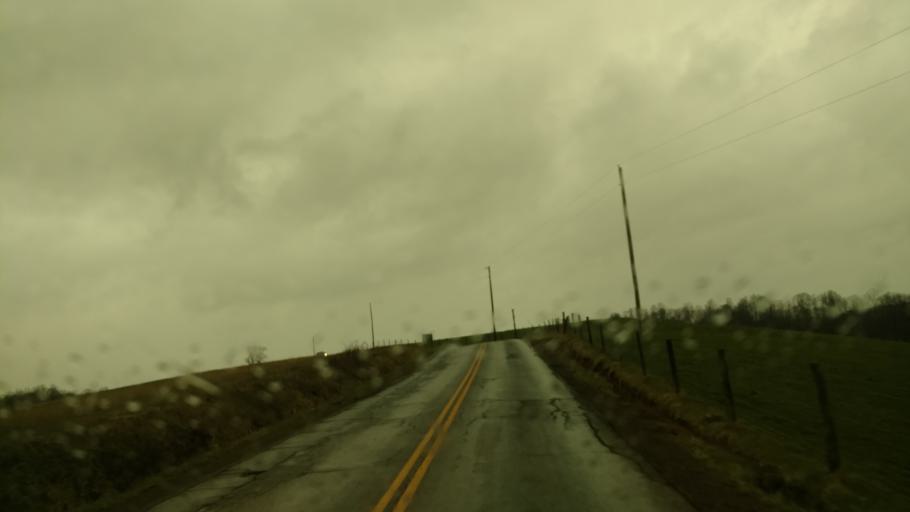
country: US
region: Ohio
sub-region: Holmes County
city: Millersburg
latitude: 40.5225
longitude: -81.8531
